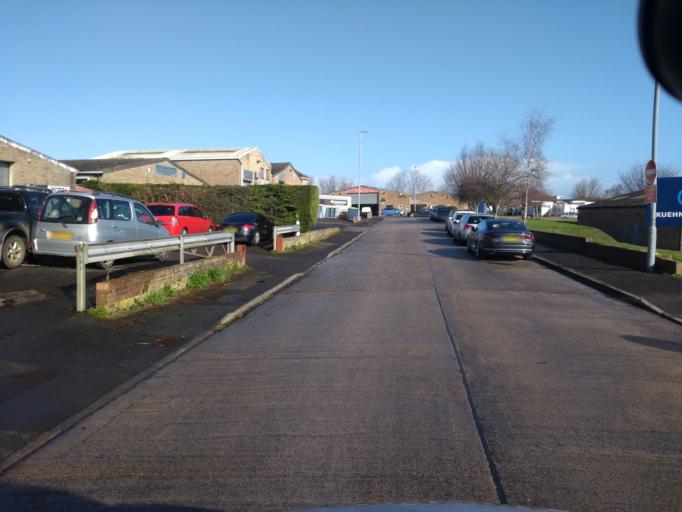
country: GB
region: England
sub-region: Somerset
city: Yeovil
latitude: 50.9521
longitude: -2.6050
